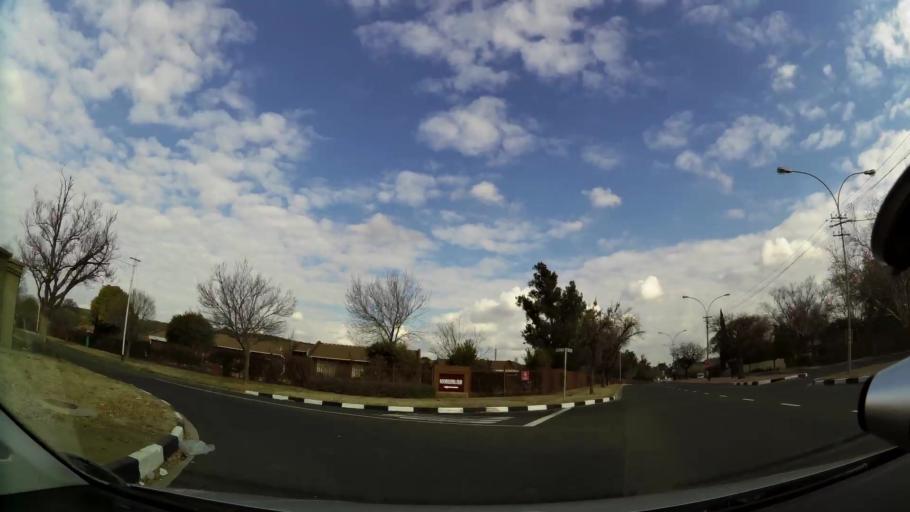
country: ZA
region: Orange Free State
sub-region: Mangaung Metropolitan Municipality
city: Bloemfontein
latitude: -29.0861
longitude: 26.2318
